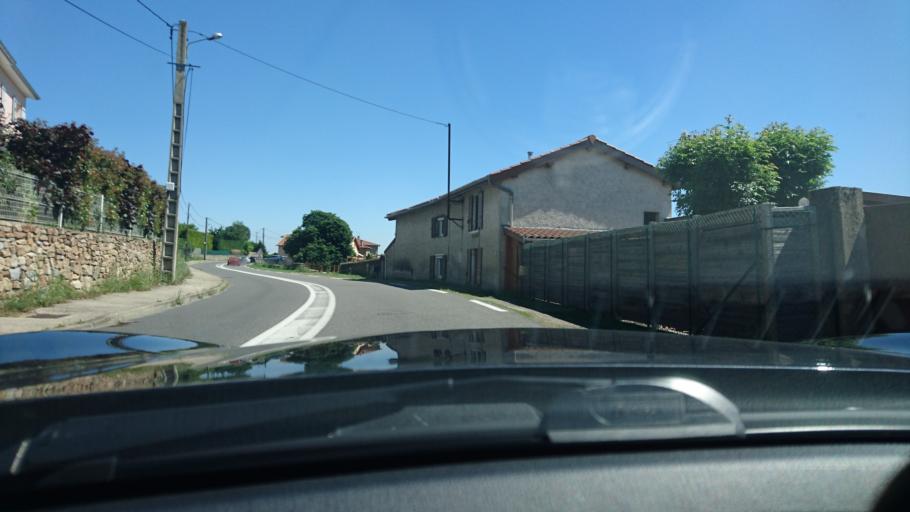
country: FR
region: Rhone-Alpes
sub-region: Departement du Rhone
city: Vaugneray
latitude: 45.7311
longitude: 4.6612
